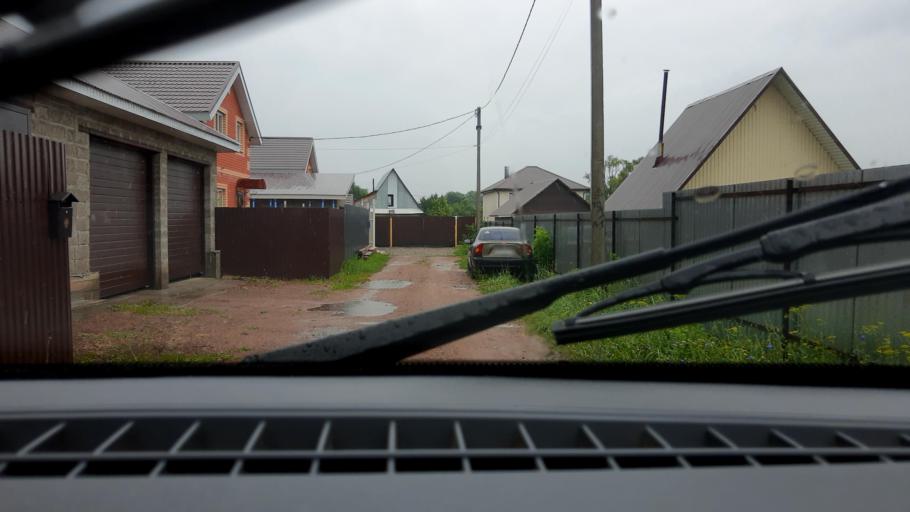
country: RU
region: Bashkortostan
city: Mikhaylovka
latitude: 54.8175
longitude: 55.8491
